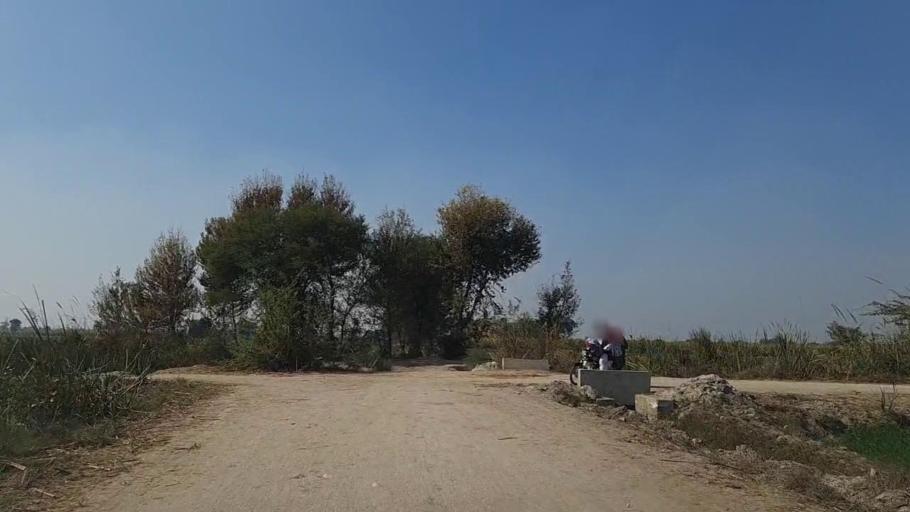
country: PK
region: Sindh
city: Daur
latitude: 26.5002
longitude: 68.3465
